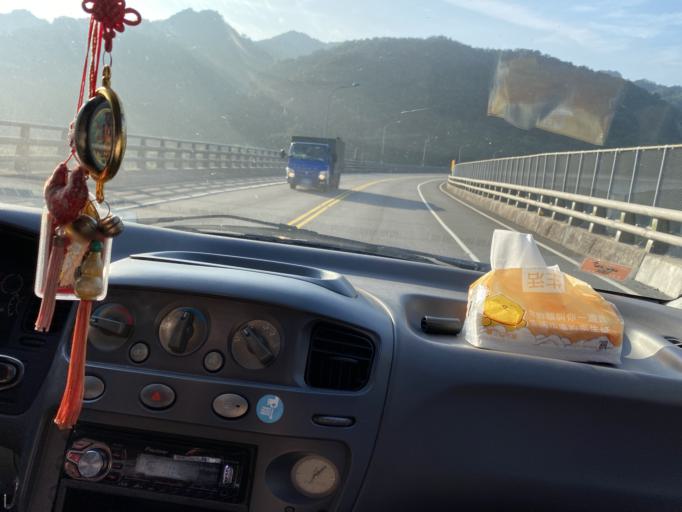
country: TW
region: Taiwan
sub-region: Keelung
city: Keelung
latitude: 25.0461
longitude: 121.7795
